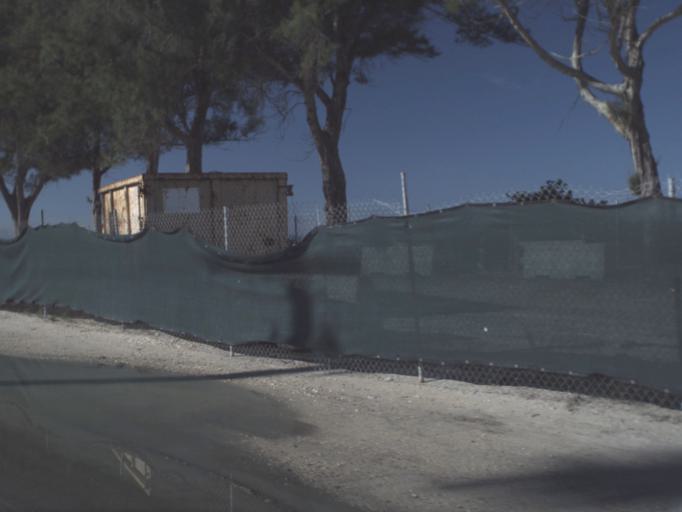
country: US
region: Florida
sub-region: Manatee County
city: Bradenton Beach
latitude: 27.4598
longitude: -82.6967
